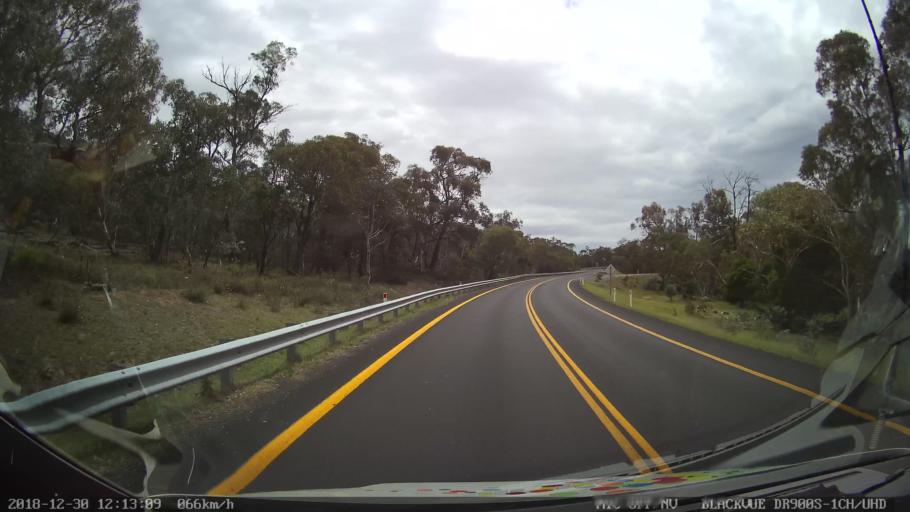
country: AU
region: New South Wales
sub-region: Snowy River
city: Jindabyne
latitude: -36.3512
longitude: 148.5853
